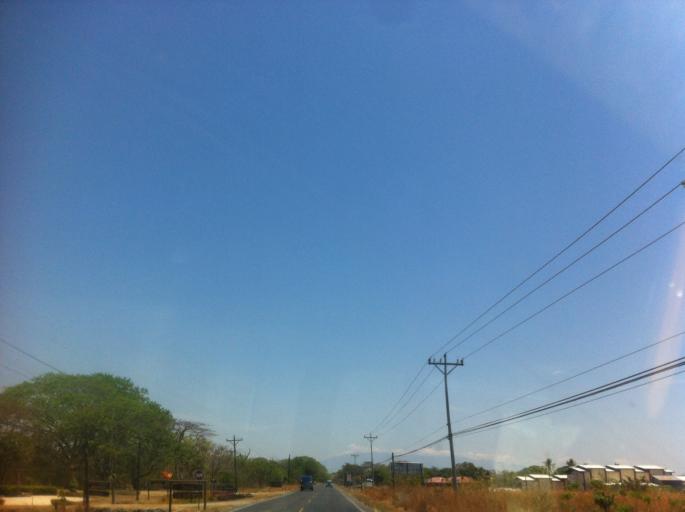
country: CR
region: Guanacaste
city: Sardinal
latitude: 10.5673
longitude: -85.5880
